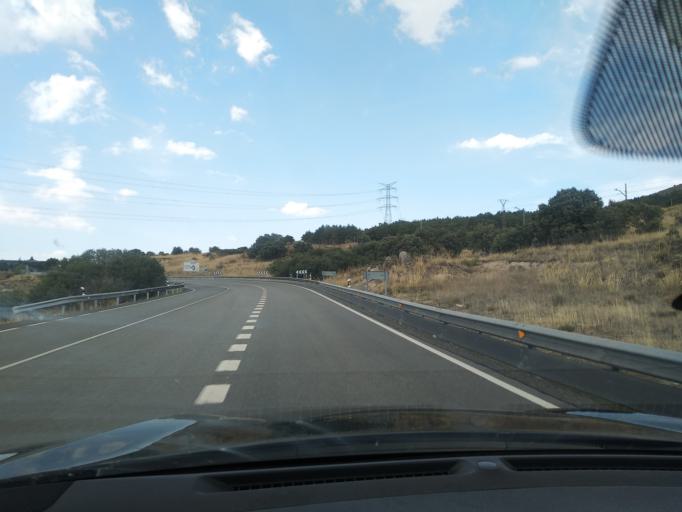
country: ES
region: Castille and Leon
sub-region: Provincia de Segovia
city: Otero de Herreros
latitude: 40.7722
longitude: -4.2021
